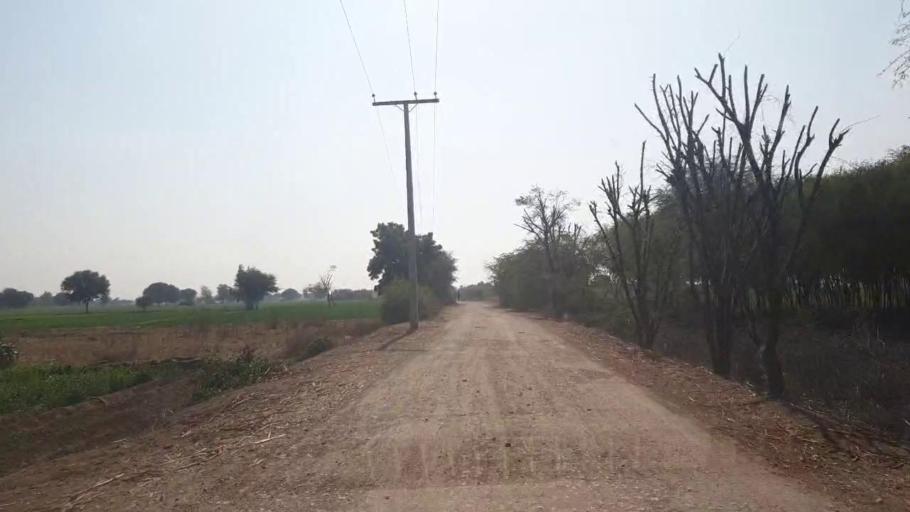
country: PK
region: Sindh
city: Shahdadpur
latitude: 26.0440
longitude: 68.4627
